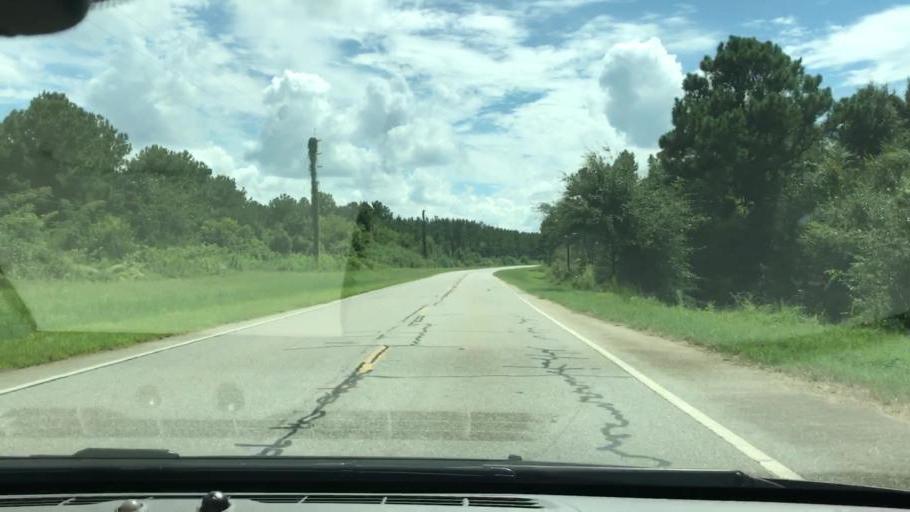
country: US
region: Georgia
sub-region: Quitman County
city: Georgetown
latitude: 32.0722
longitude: -85.0370
